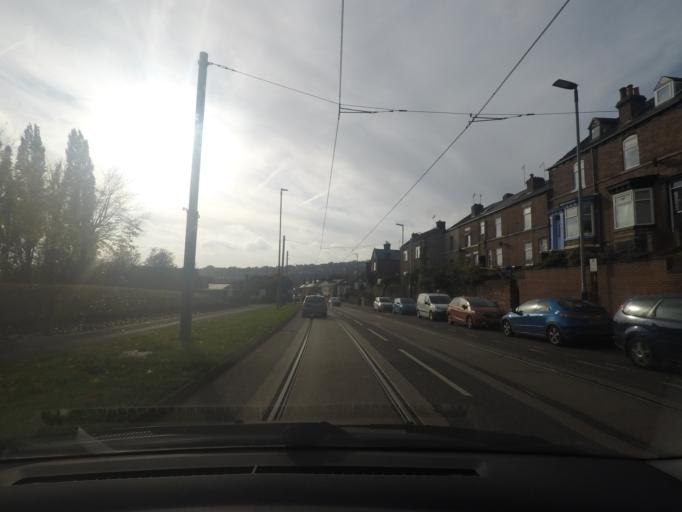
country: GB
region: England
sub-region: Sheffield
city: Sheffield
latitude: 53.4059
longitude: -1.5042
